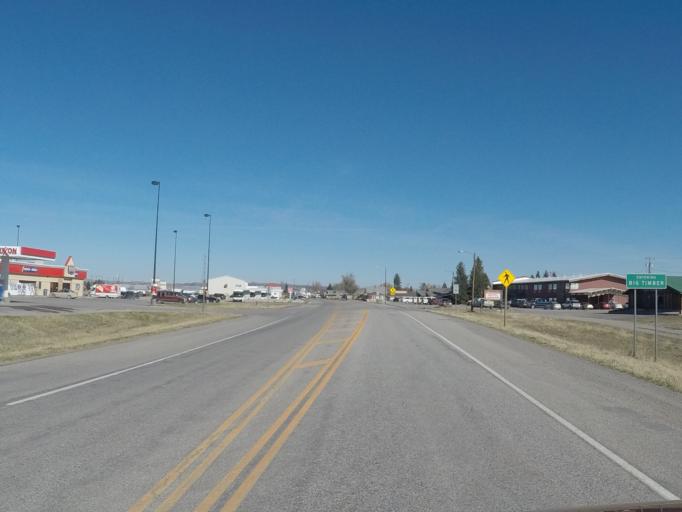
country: US
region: Montana
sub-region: Sweet Grass County
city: Big Timber
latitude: 45.8312
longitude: -109.9621
